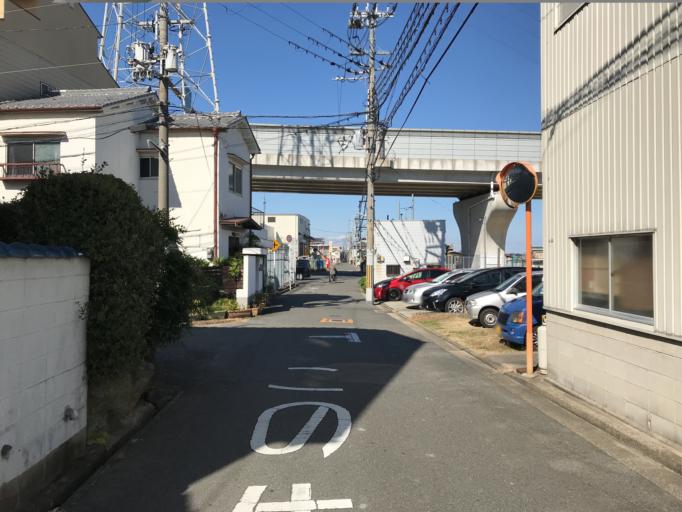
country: JP
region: Osaka
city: Tondabayashicho
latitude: 34.5362
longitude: 135.6110
